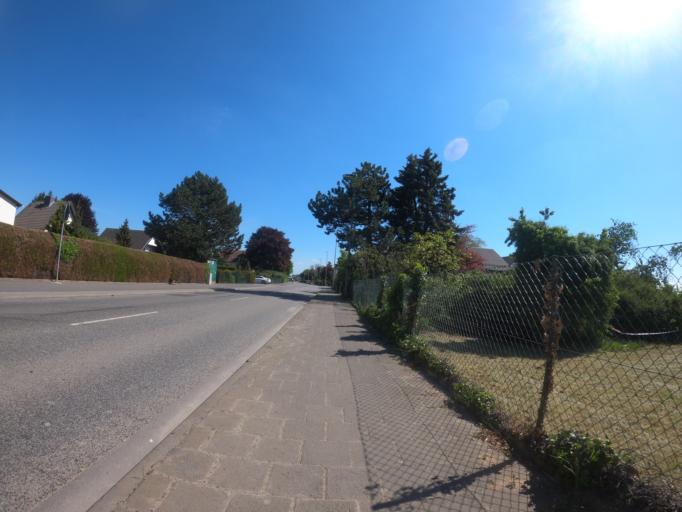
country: DE
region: Hesse
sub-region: Regierungsbezirk Darmstadt
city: Florsheim
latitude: 50.0211
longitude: 8.4180
